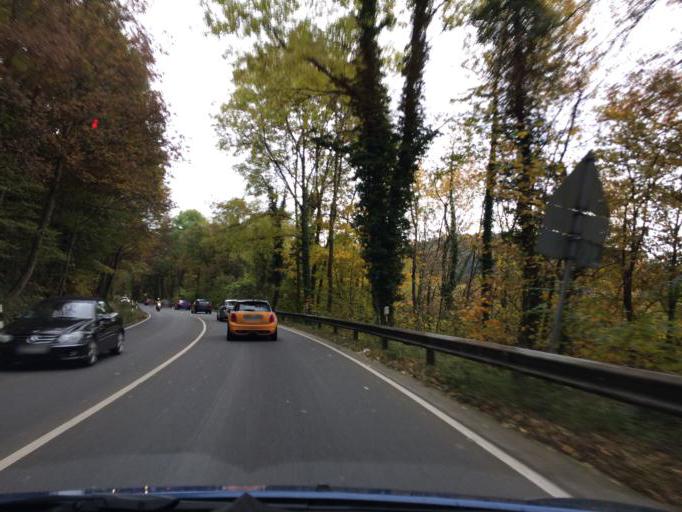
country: DE
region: North Rhine-Westphalia
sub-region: Regierungsbezirk Koln
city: Bad Honnef
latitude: 50.6785
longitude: 7.2447
